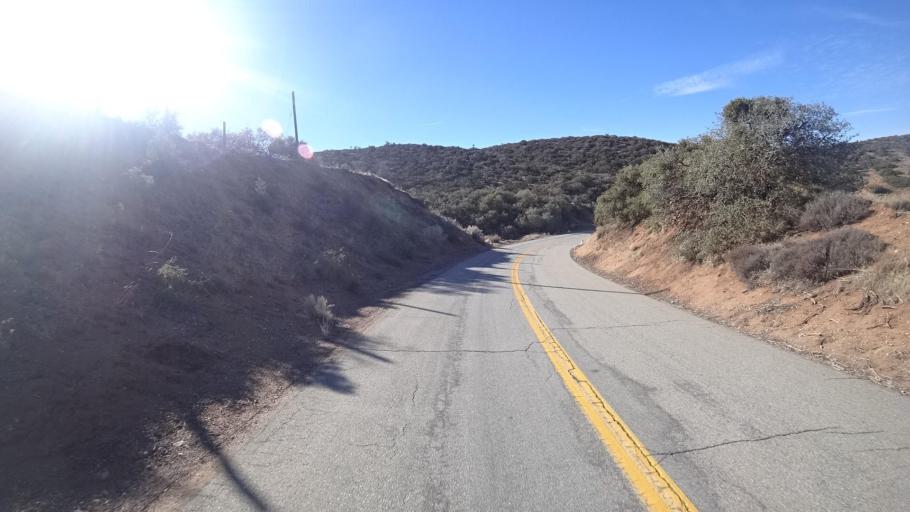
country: US
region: California
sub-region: Kern County
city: Maricopa
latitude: 34.8790
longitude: -119.3545
